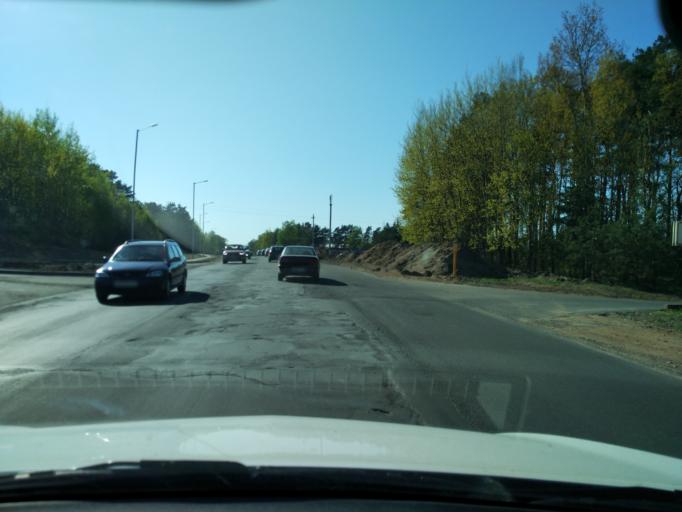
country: BY
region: Minsk
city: Borovlyany
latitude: 53.9648
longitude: 27.6686
